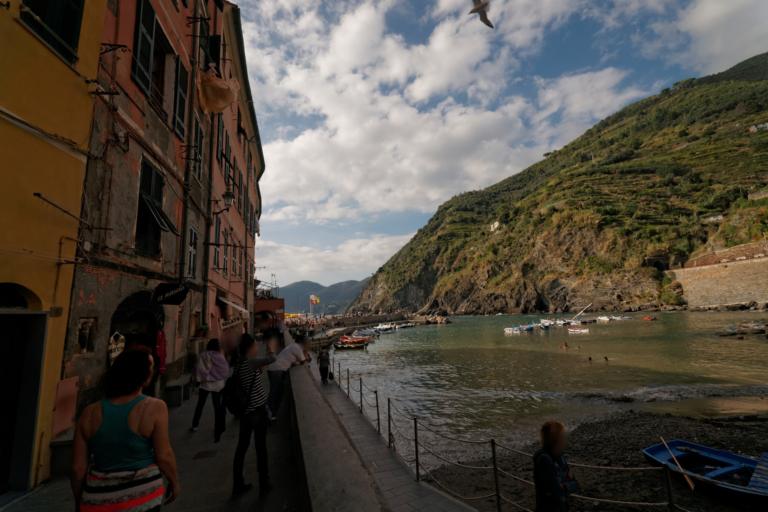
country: IT
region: Liguria
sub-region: Provincia di La Spezia
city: Vernazza
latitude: 44.1348
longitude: 9.6825
